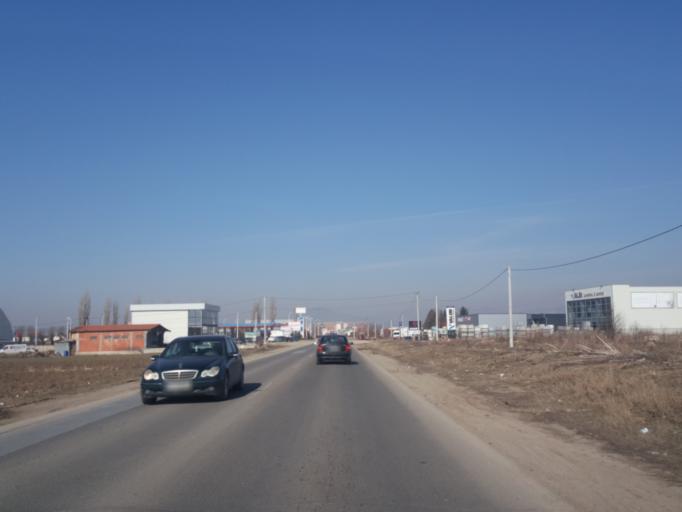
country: XK
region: Mitrovica
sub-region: Vushtrri
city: Vushtrri
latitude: 42.8070
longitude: 20.9897
